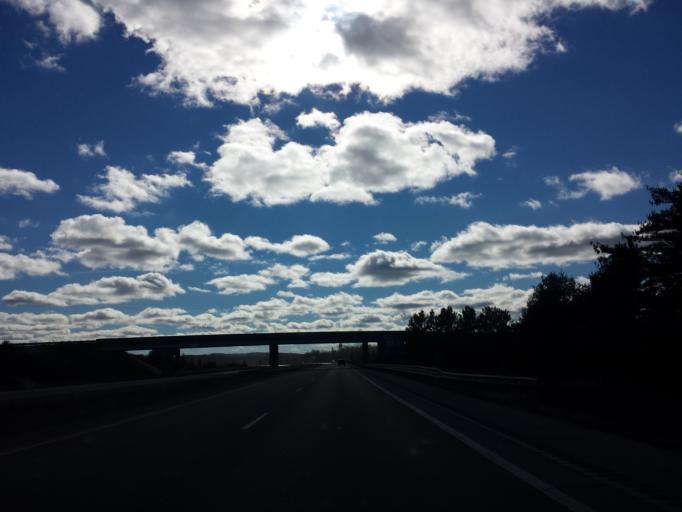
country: US
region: Michigan
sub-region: Cheboygan County
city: Indian River
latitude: 45.4122
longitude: -84.6047
